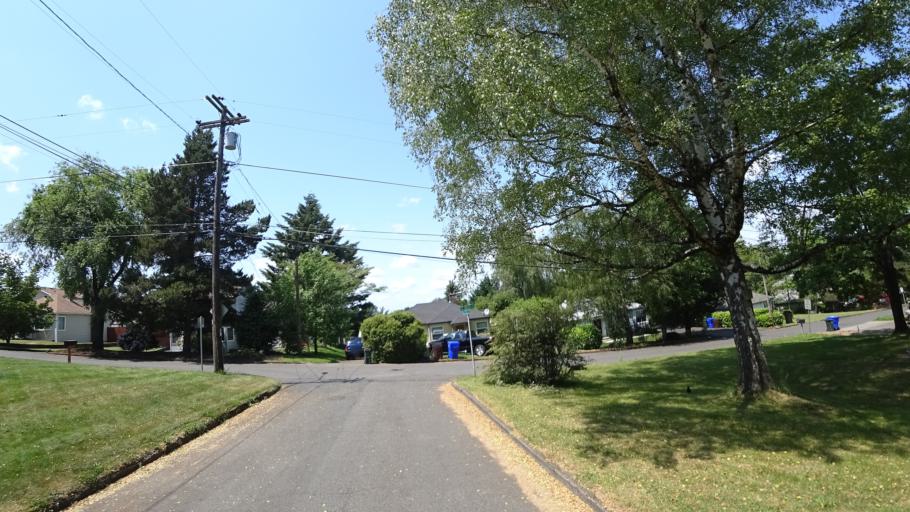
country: US
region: Oregon
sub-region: Multnomah County
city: Lents
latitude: 45.4622
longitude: -122.5645
